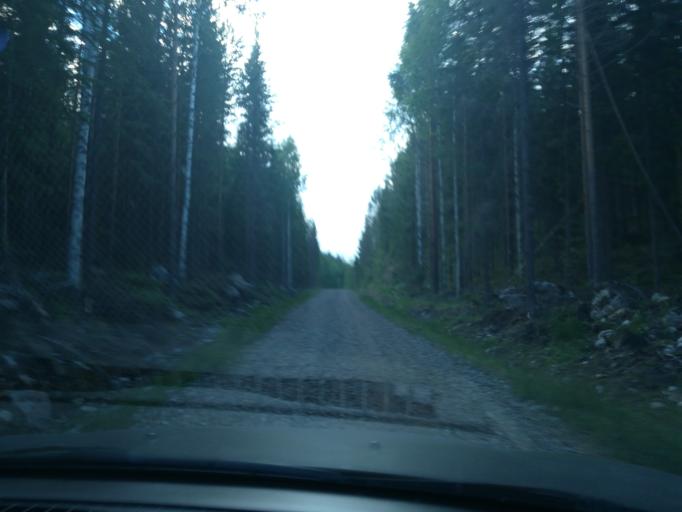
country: FI
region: Southern Savonia
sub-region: Mikkeli
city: Puumala
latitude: 61.6206
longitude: 28.1734
